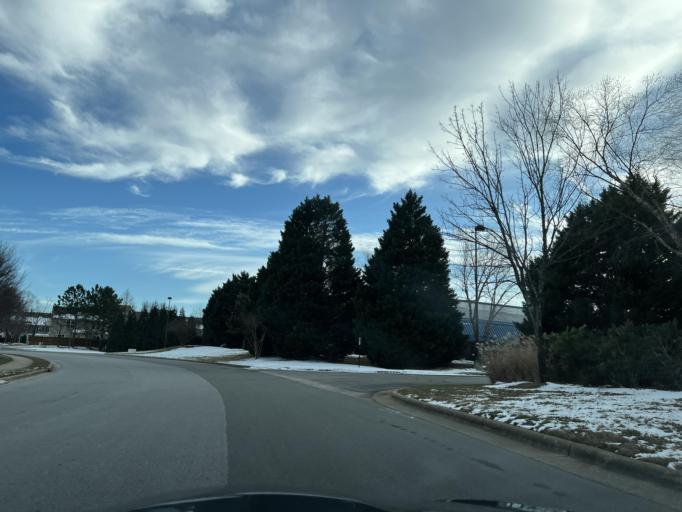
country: US
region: North Carolina
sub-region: Wake County
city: Raleigh
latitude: 35.8694
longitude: -78.5921
